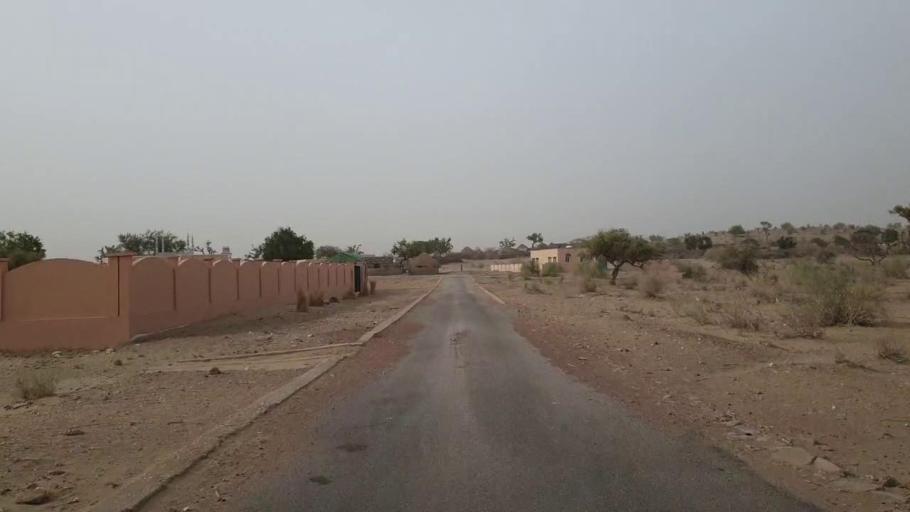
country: PK
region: Sindh
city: Islamkot
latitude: 24.5733
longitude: 70.3655
